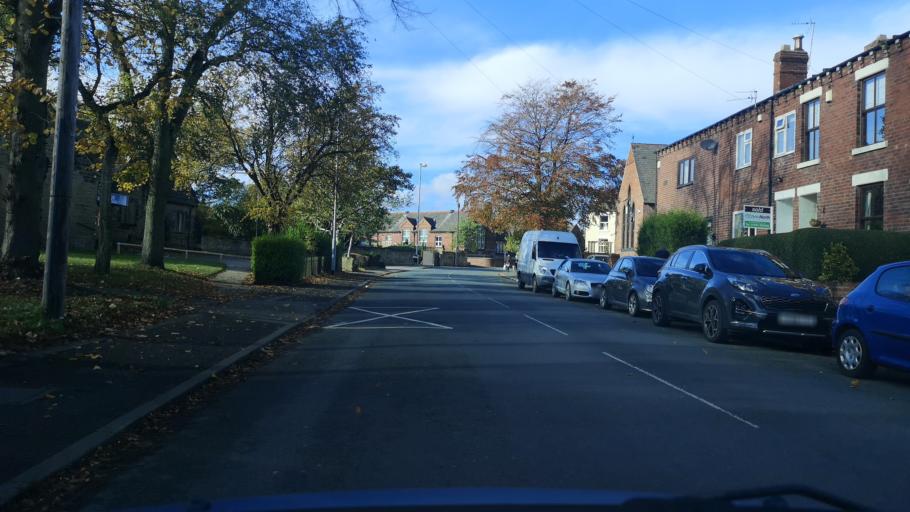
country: GB
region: England
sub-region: City and Borough of Wakefield
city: Normanton
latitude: 53.6981
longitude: -1.4132
